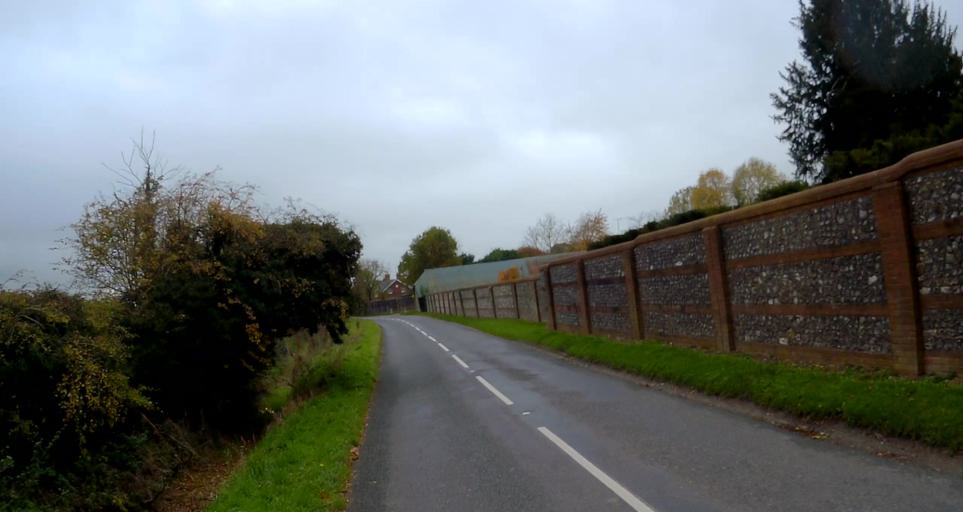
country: GB
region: England
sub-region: Hampshire
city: Overton
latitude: 51.1512
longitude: -1.1716
